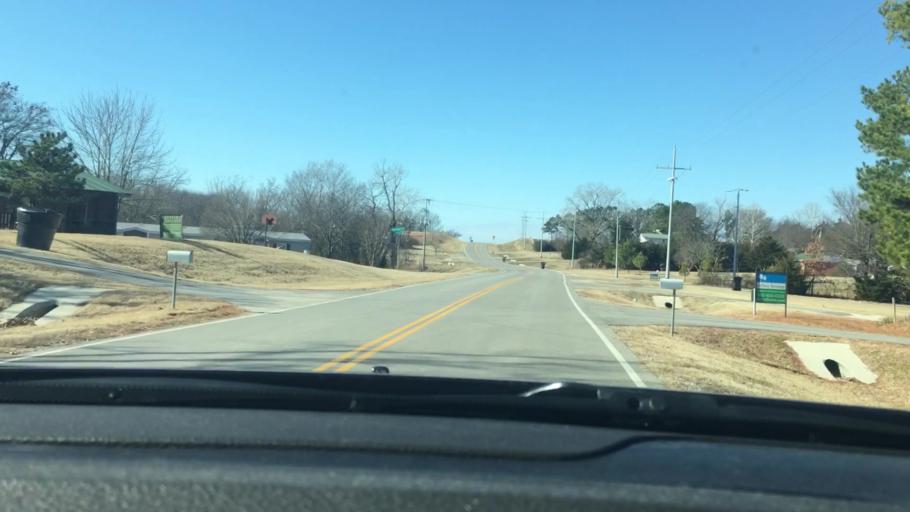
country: US
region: Oklahoma
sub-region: Murray County
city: Davis
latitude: 34.4771
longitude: -97.0504
